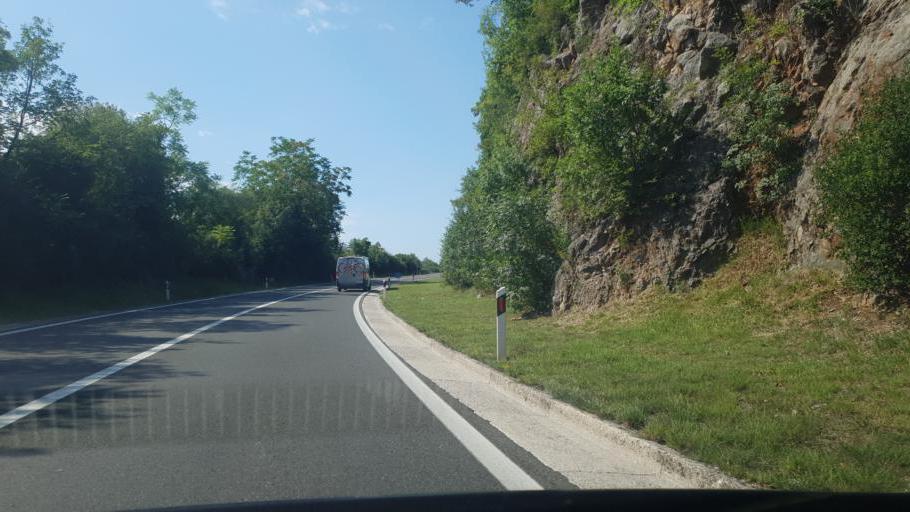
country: HR
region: Primorsko-Goranska
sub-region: Grad Opatija
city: Opatija
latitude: 45.3498
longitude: 14.3067
